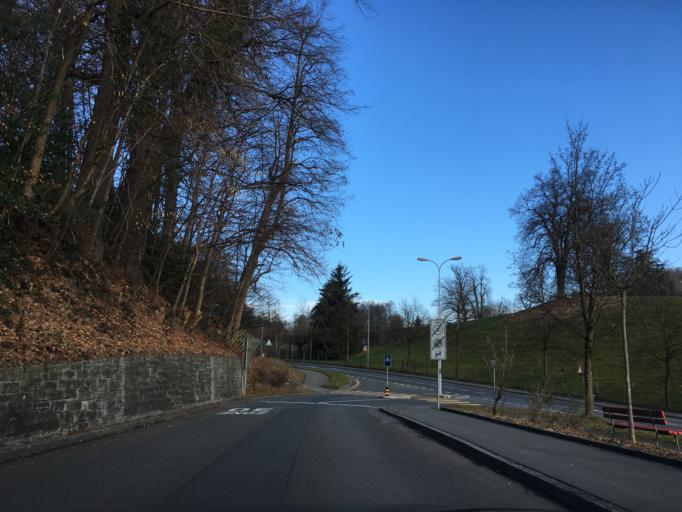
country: CH
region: Lucerne
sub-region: Lucerne-Stadt District
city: Luzern
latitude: 47.0588
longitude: 8.3238
